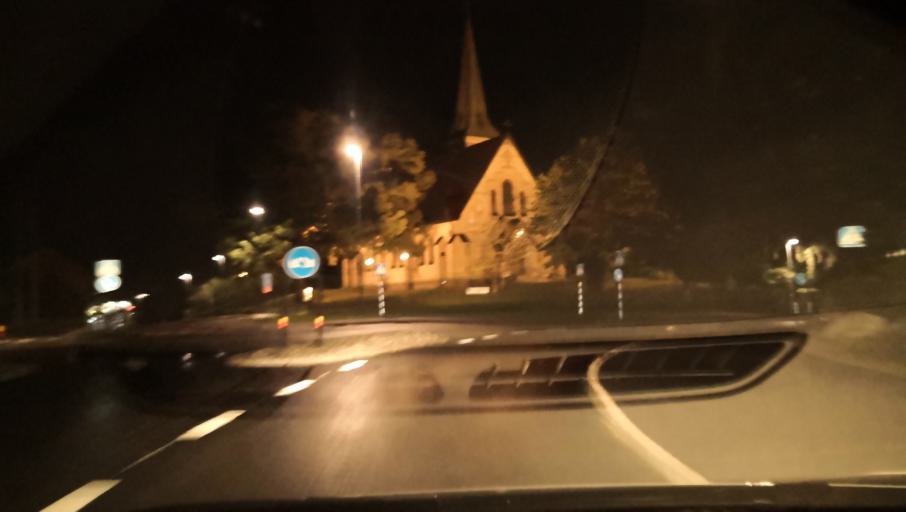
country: SE
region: Stockholm
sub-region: Varmdo Kommun
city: Gustavsberg
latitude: 59.3271
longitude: 18.3848
